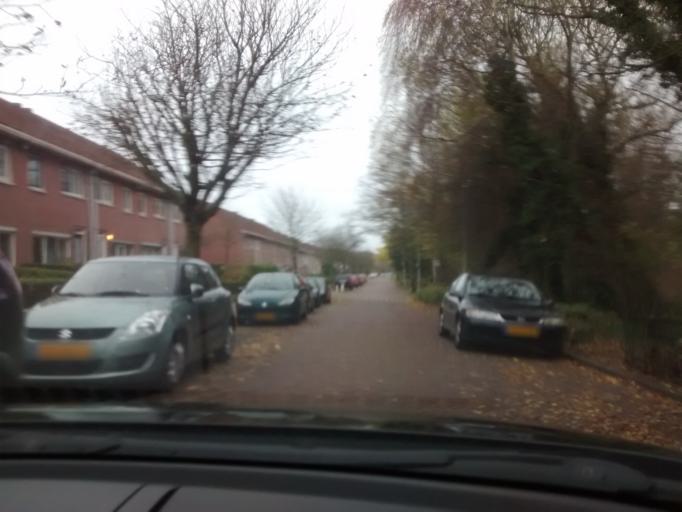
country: NL
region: South Holland
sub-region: Gemeente Katwijk
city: Katwijk aan den Rijn
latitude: 52.1956
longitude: 4.4197
